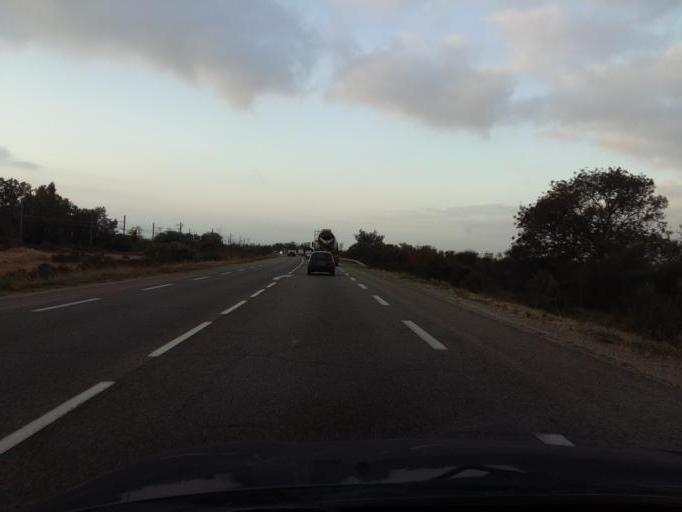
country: FR
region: Provence-Alpes-Cote d'Azur
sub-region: Departement des Bouches-du-Rhone
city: Istres
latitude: 43.5519
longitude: 4.9583
